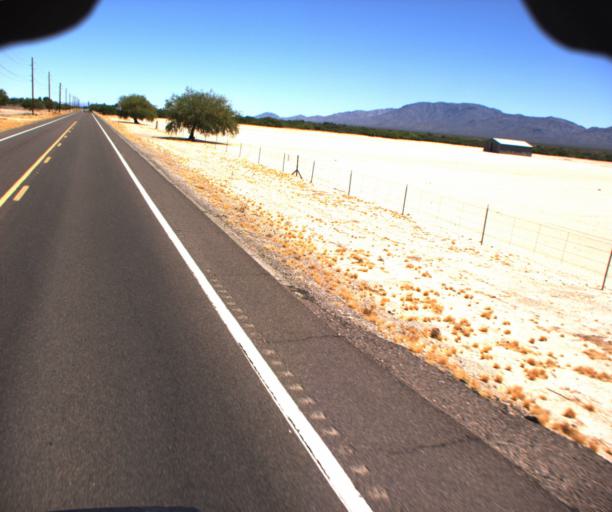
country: US
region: Arizona
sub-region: La Paz County
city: Salome
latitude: 33.8143
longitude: -113.5558
